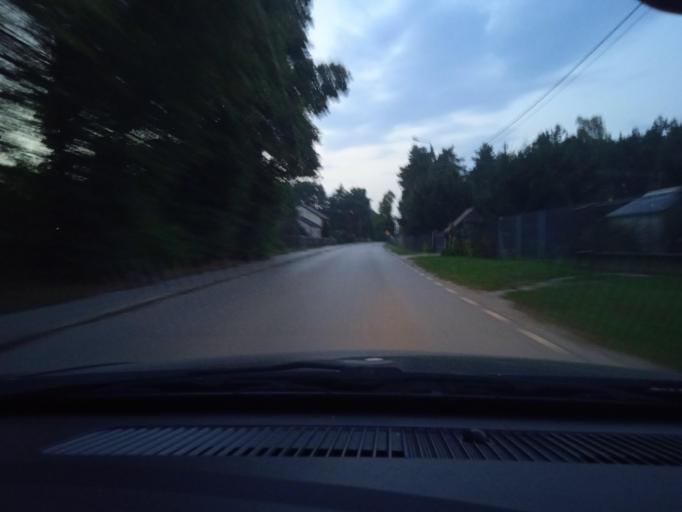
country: PL
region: Masovian Voivodeship
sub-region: Powiat plonski
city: Joniec
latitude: 52.5631
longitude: 20.6690
